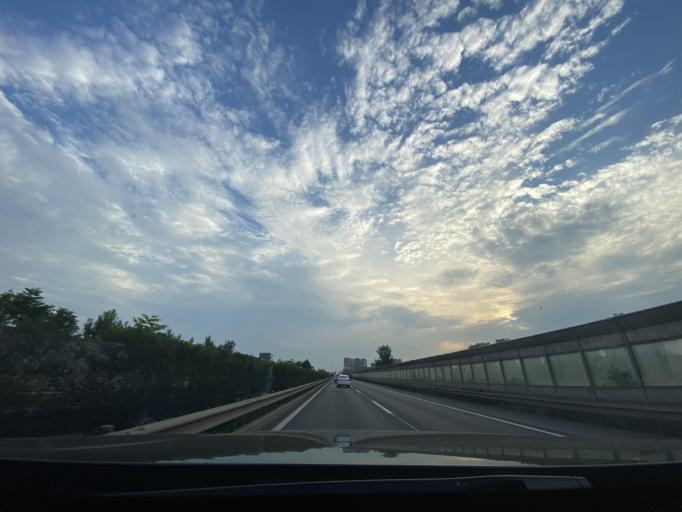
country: CN
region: Sichuan
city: Deyang
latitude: 31.0838
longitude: 104.4015
